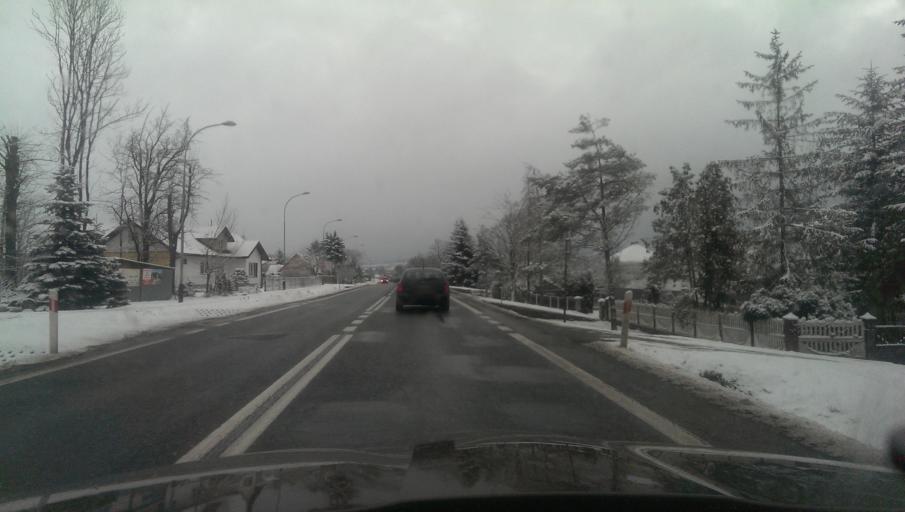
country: PL
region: Subcarpathian Voivodeship
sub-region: Powiat krosnienski
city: Miejsce Piastowe
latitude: 49.6104
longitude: 21.8027
